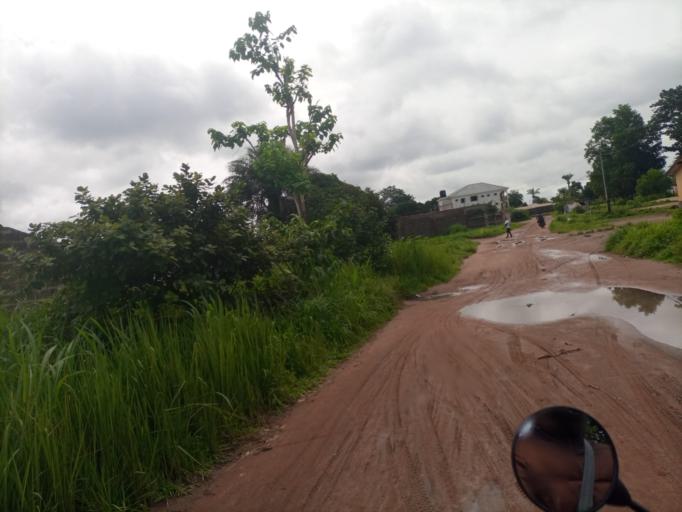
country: SL
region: Northern Province
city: Sawkta
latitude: 8.6244
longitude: -13.2018
